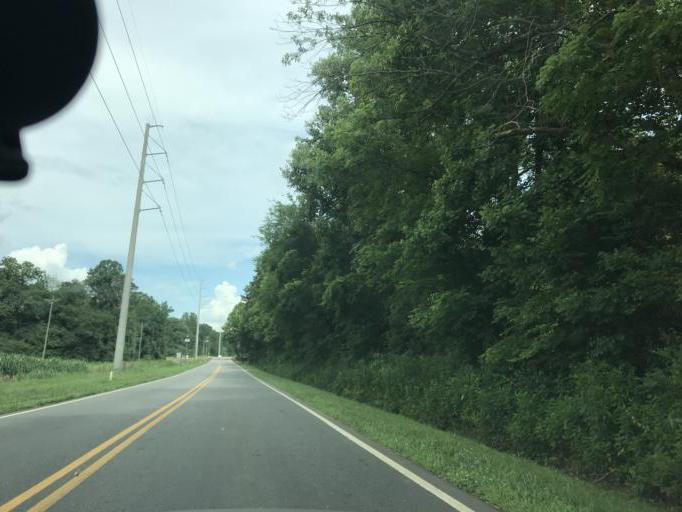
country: US
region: Georgia
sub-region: Forsyth County
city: Cumming
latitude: 34.3091
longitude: -84.2234
